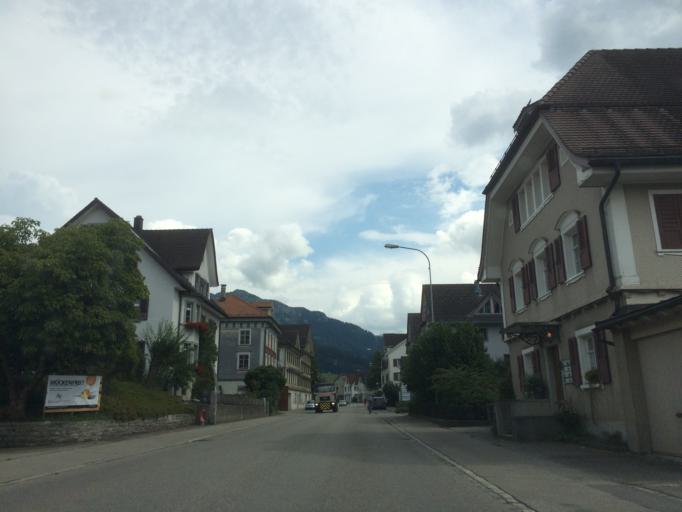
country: CH
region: Saint Gallen
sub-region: Wahlkreis Toggenburg
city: Krummenau
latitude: 47.2309
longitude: 9.1923
